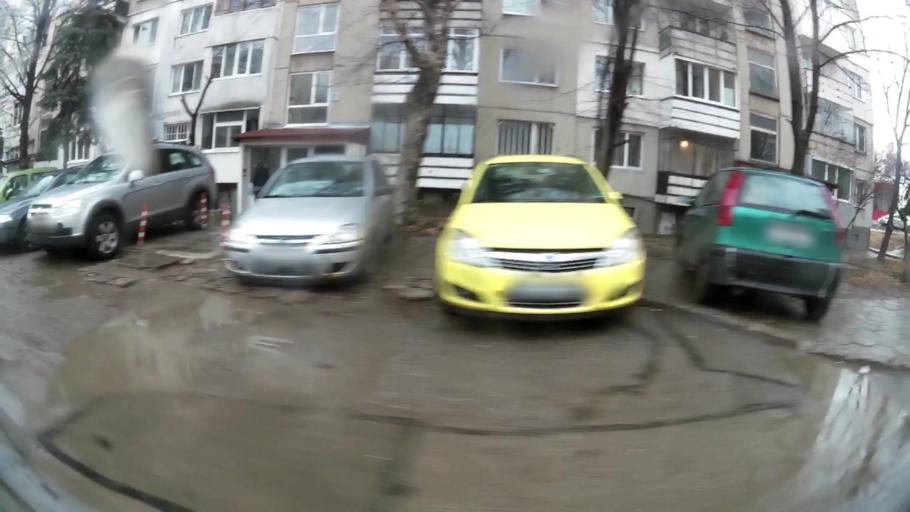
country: BG
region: Sofia-Capital
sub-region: Stolichna Obshtina
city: Sofia
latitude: 42.6441
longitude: 23.3733
